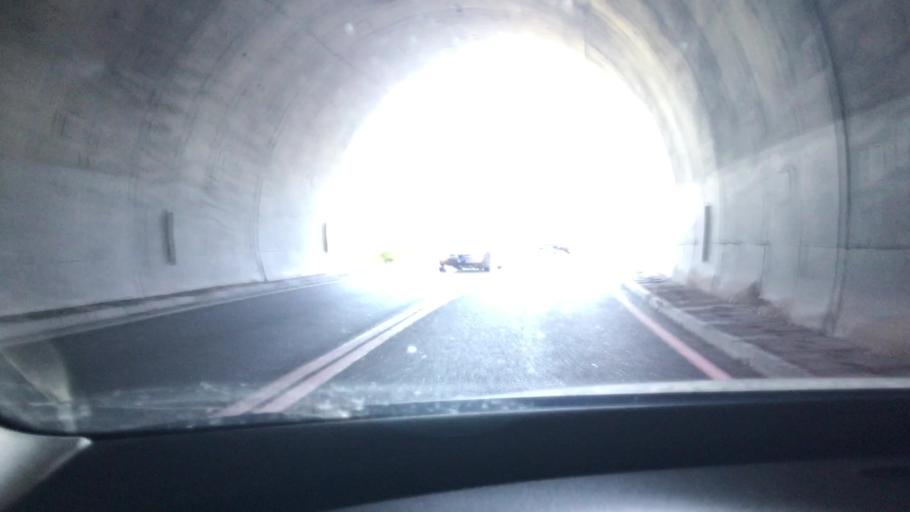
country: BA
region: Federation of Bosnia and Herzegovina
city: Jablanica
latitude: 43.6857
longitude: 17.7906
